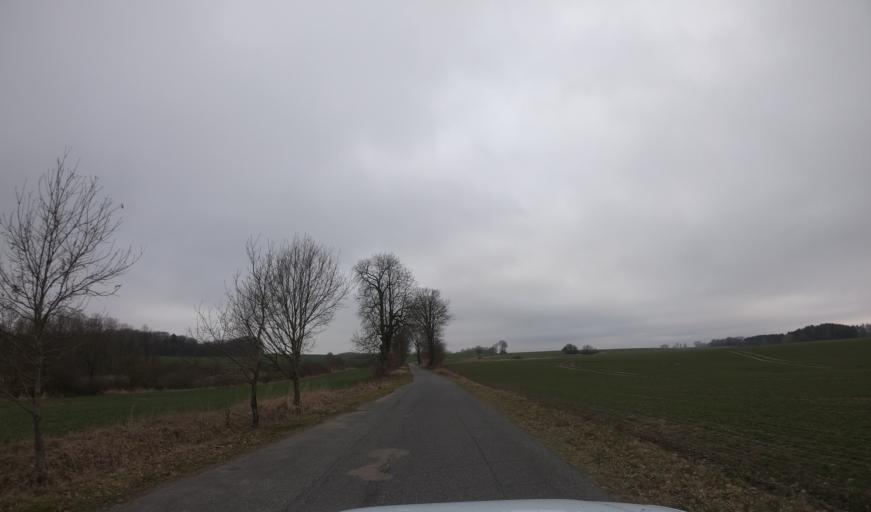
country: PL
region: West Pomeranian Voivodeship
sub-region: Powiat gryficki
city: Ploty
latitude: 53.8510
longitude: 15.2705
